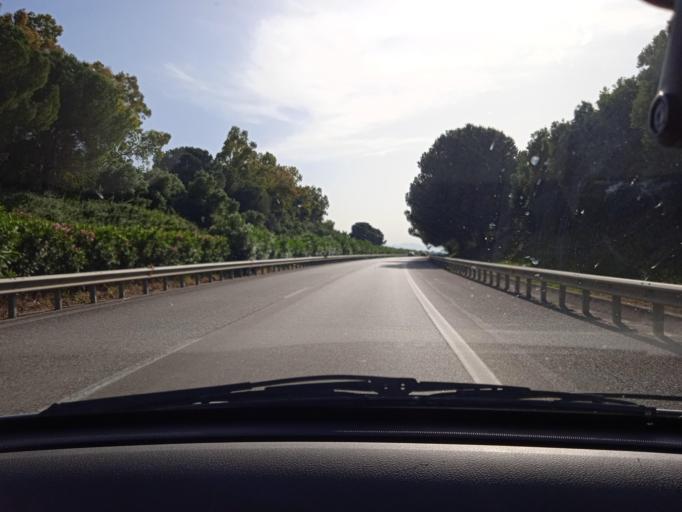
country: IT
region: Sicily
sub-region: Messina
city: Acquedolci
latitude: 38.0533
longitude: 14.5993
